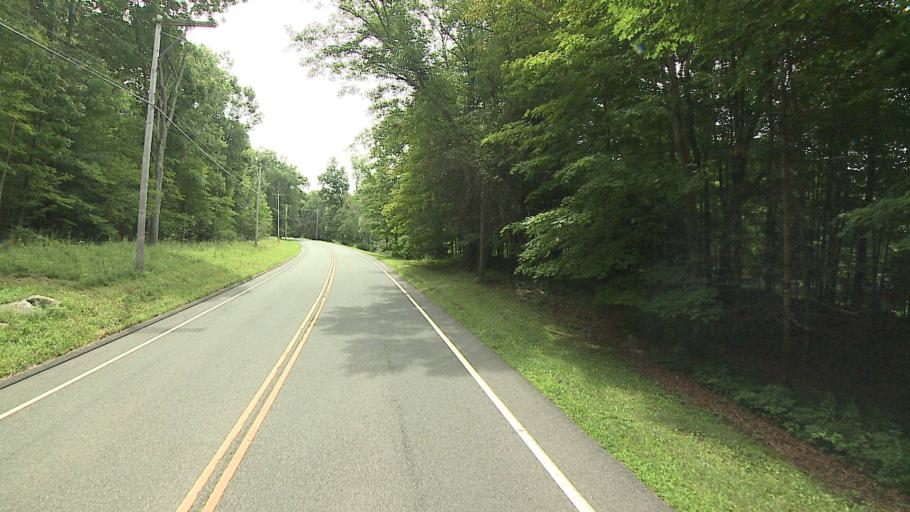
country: US
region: Connecticut
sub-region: Litchfield County
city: New Milford
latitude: 41.5735
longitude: -73.3187
